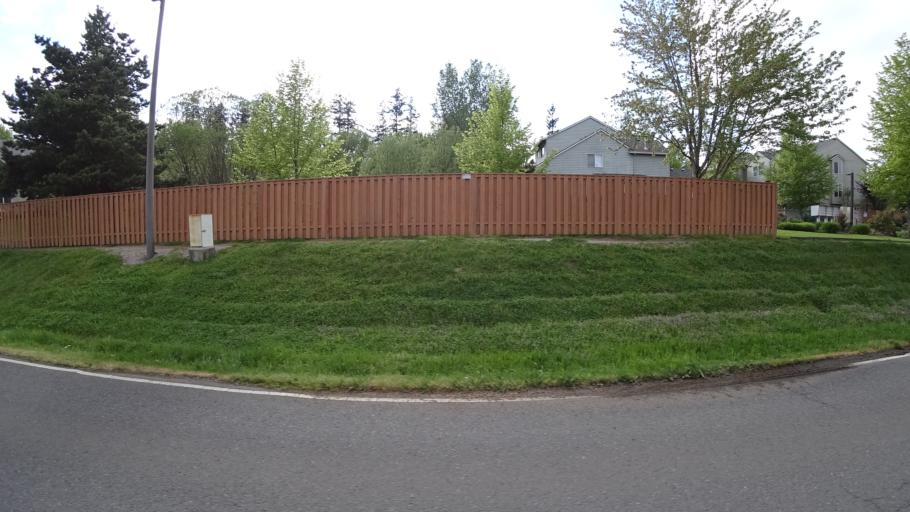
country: US
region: Oregon
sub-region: Washington County
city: Beaverton
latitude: 45.4520
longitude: -122.8363
